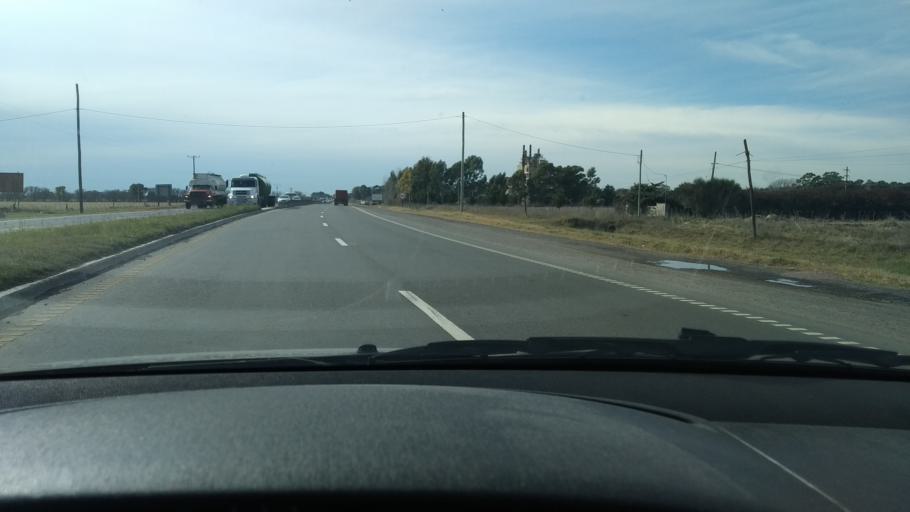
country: AR
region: Buenos Aires
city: Olavarria
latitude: -36.9155
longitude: -60.2033
